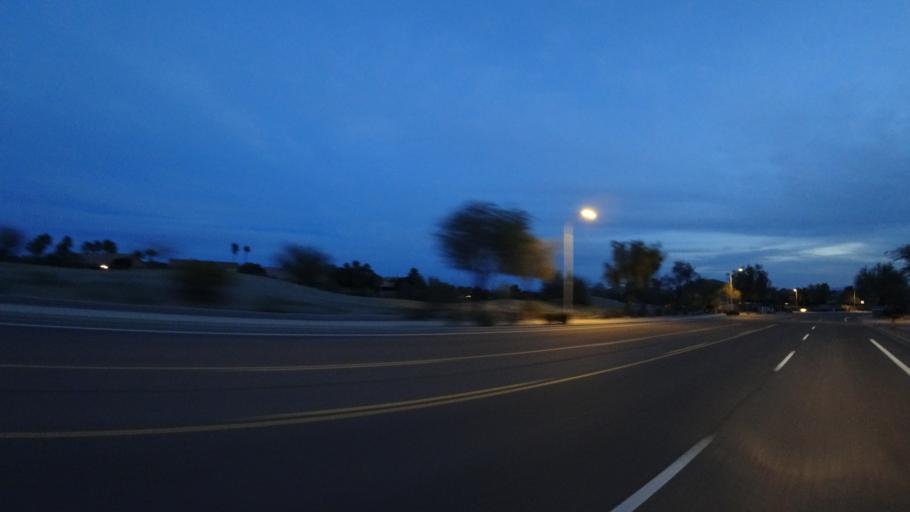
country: US
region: Arizona
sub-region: Maricopa County
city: Laveen
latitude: 33.3012
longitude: -112.0952
